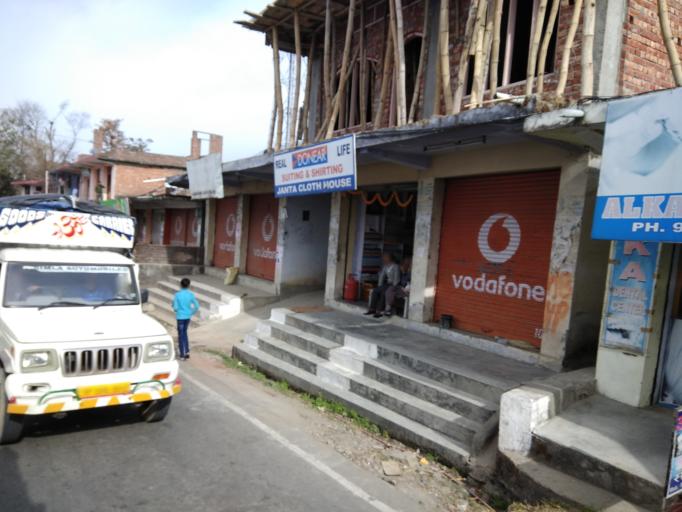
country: IN
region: Himachal Pradesh
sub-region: Kangra
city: Dharmsala
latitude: 32.1715
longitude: 76.3892
